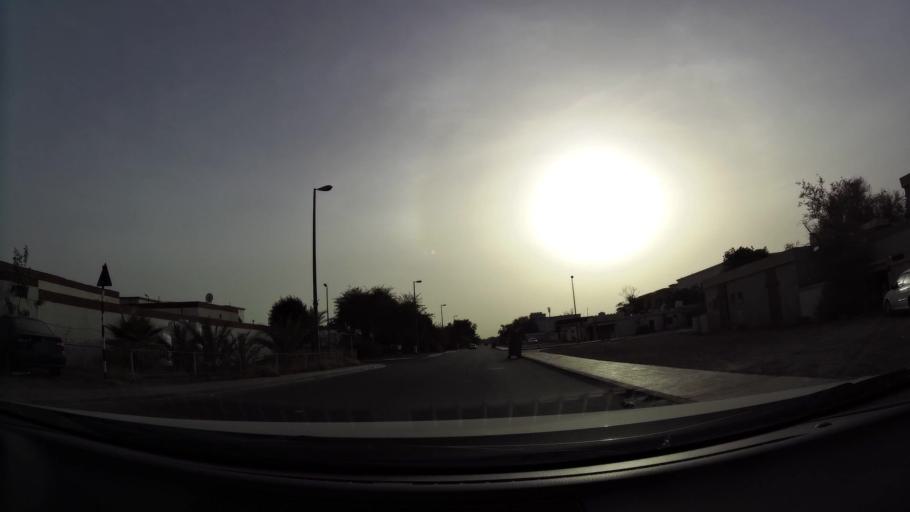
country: OM
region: Al Buraimi
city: Al Buraymi
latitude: 24.2452
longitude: 55.7497
